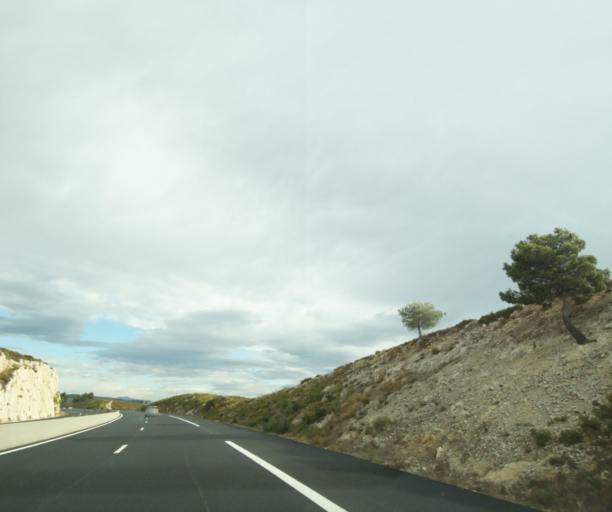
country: FR
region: Provence-Alpes-Cote d'Azur
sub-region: Departement des Bouches-du-Rhone
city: Carry-le-Rouet
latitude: 43.3393
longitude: 5.1380
